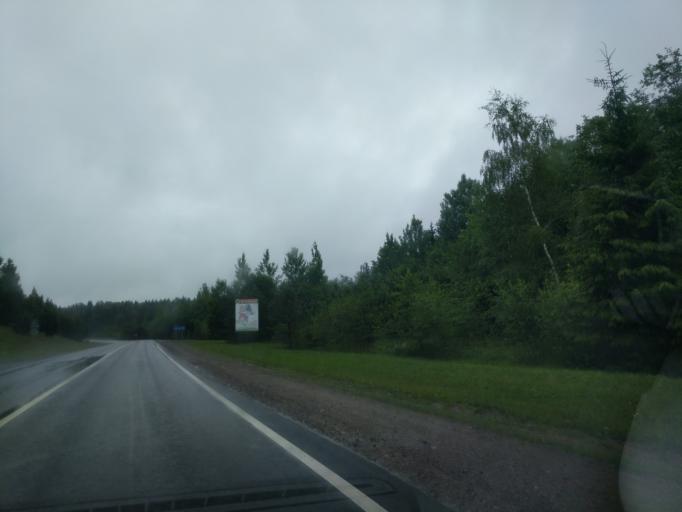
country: BY
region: Minsk
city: Bal'shavik
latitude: 54.1084
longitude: 27.5295
